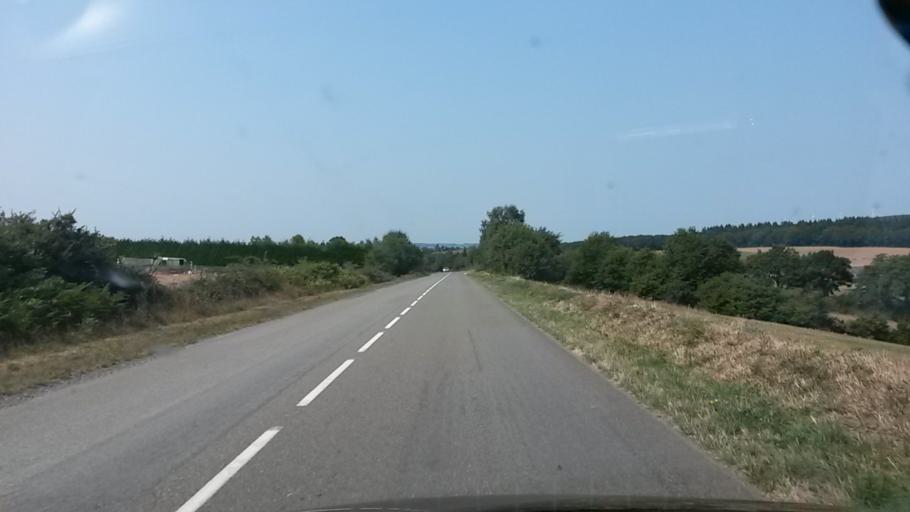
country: FR
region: Pays de la Loire
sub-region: Departement de la Mayenne
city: Villaines-la-Juhel
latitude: 48.3593
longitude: -0.2267
